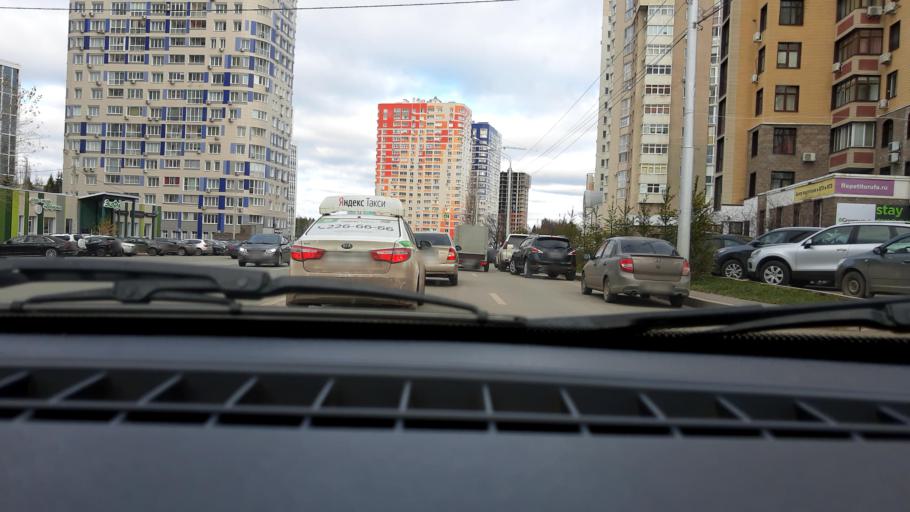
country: RU
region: Bashkortostan
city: Ufa
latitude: 54.7677
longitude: 56.0110
